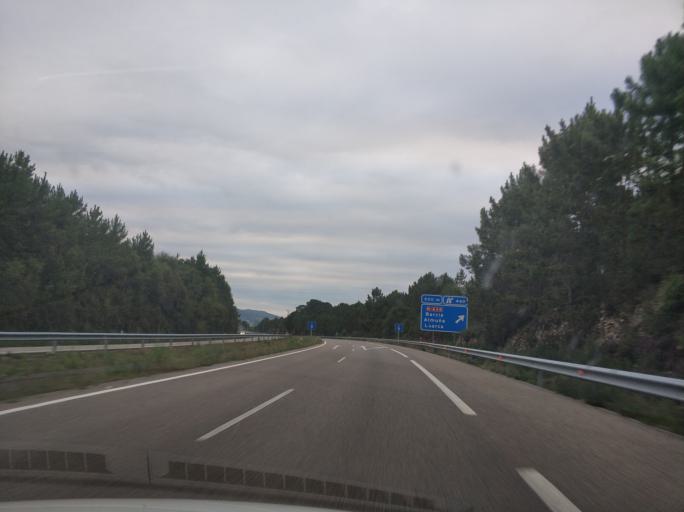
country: ES
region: Asturias
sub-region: Province of Asturias
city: Tineo
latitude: 43.5351
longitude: -6.4927
